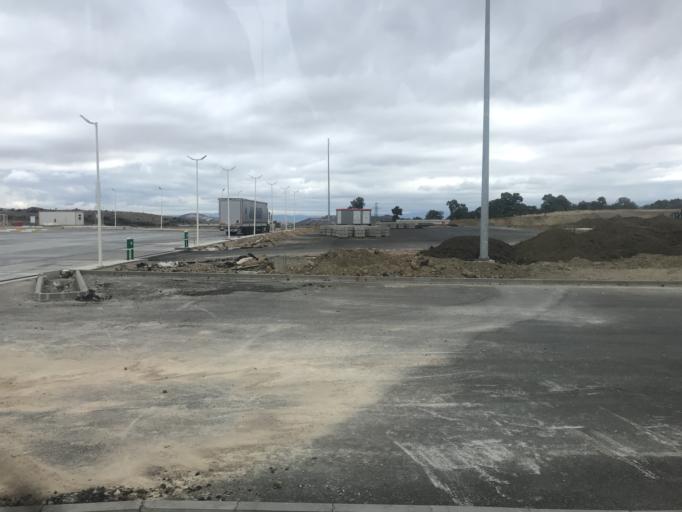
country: TR
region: Balikesir
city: Yenikoy
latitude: 39.7566
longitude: 27.9624
